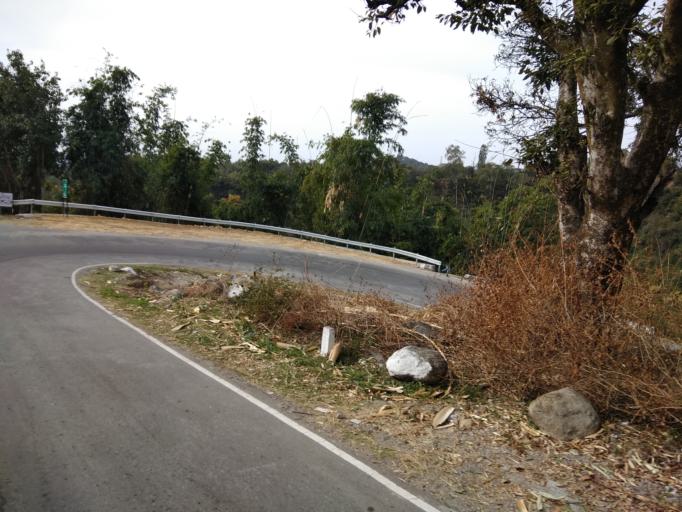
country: IN
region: Himachal Pradesh
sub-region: Kangra
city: Dharmsala
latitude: 32.1575
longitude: 76.4061
